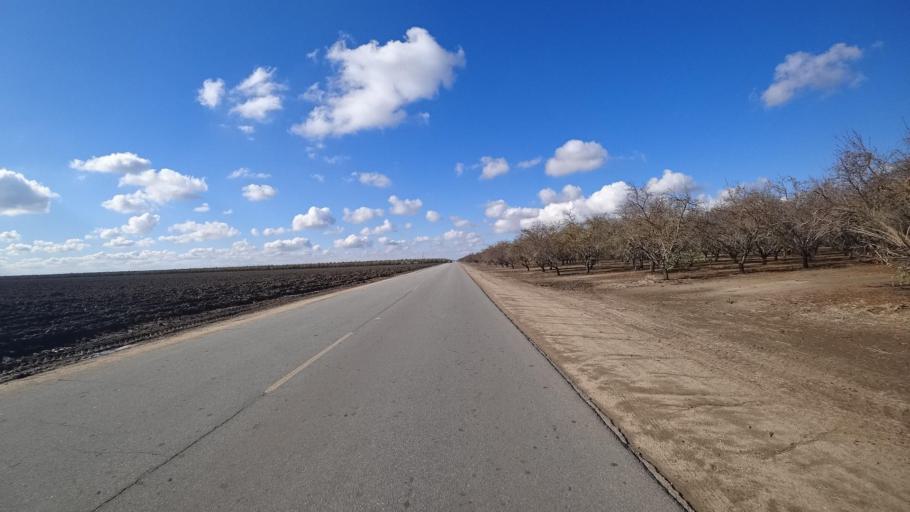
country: US
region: California
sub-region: Kern County
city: McFarland
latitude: 35.6742
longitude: -119.2900
